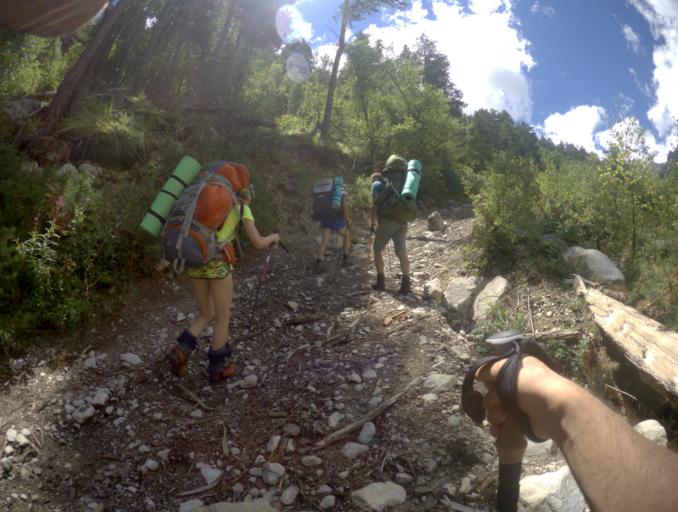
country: RU
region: Karachayevo-Cherkesiya
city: Uchkulan
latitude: 43.3549
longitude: 42.1760
